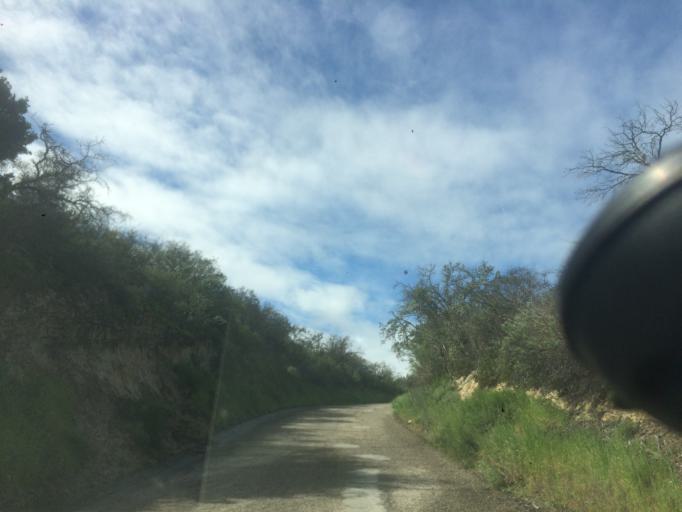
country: US
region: California
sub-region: San Luis Obispo County
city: Nipomo
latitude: 35.2098
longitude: -120.4446
